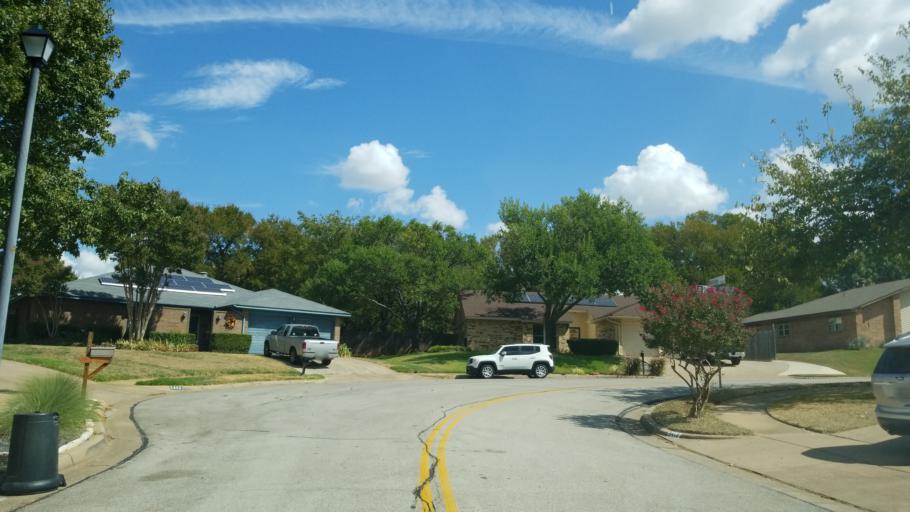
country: US
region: Texas
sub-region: Tarrant County
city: Euless
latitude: 32.8589
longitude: -97.1093
